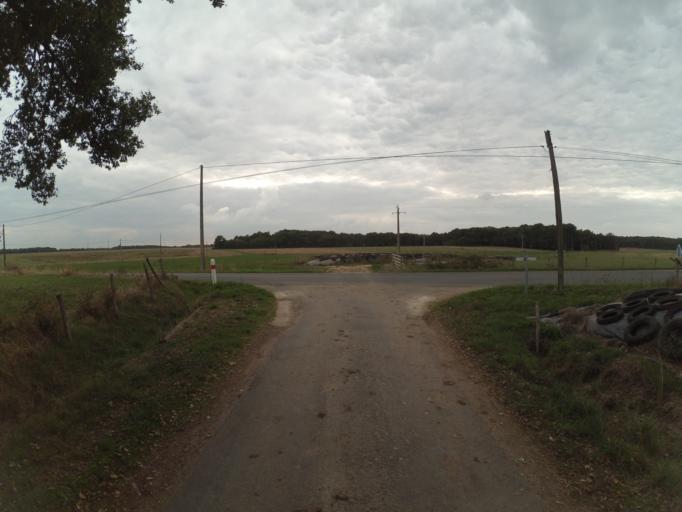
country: FR
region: Centre
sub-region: Departement d'Indre-et-Loire
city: Auzouer-en-Touraine
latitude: 47.4962
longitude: 0.9318
